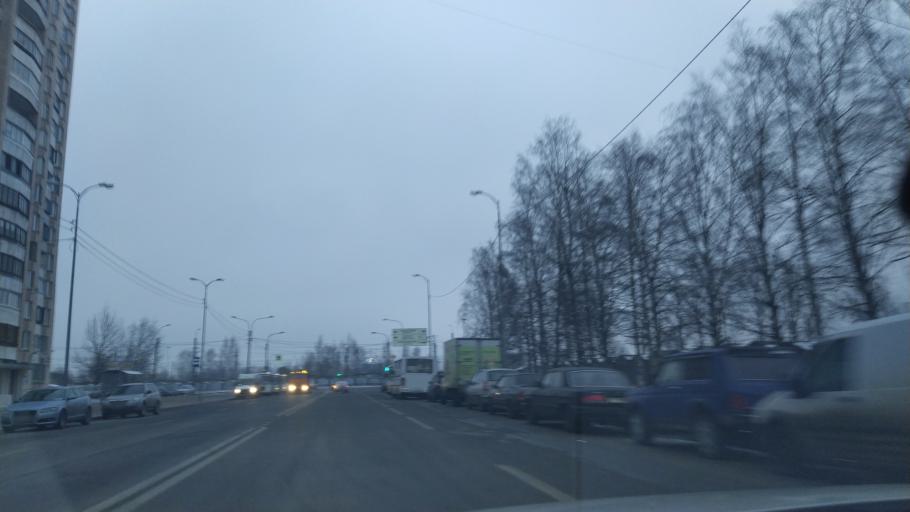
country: RU
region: St.-Petersburg
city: Grazhdanka
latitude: 60.0490
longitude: 30.3919
